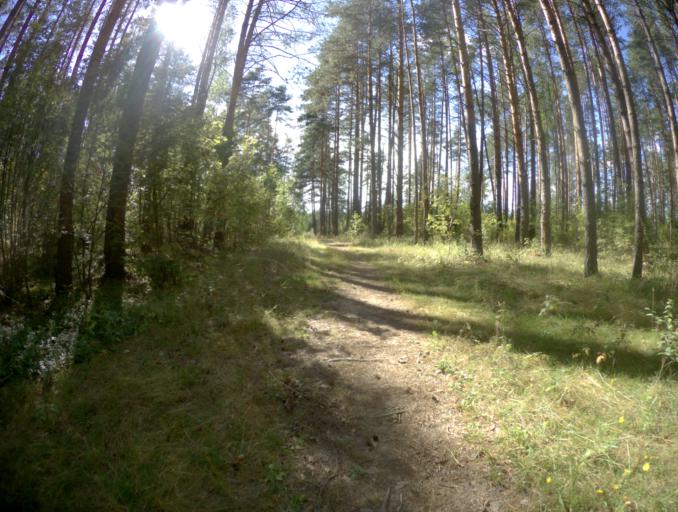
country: RU
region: Vladimir
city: Krasnaya Gorbatka
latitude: 55.8676
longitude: 41.7368
